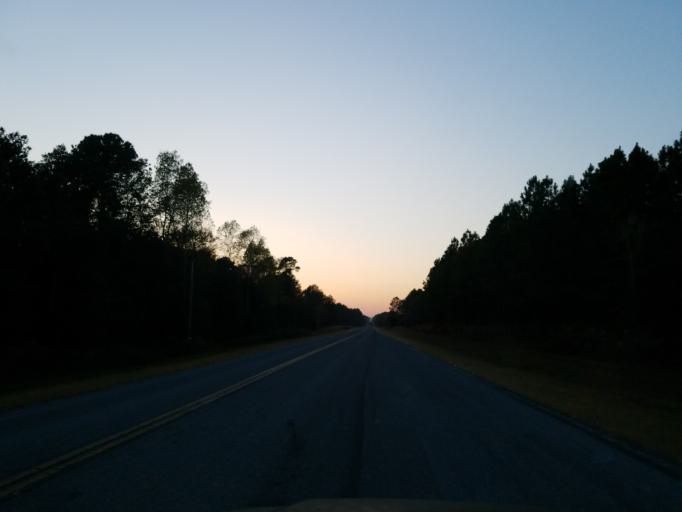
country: US
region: Georgia
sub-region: Ben Hill County
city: Fitzgerald
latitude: 31.7209
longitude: -83.4357
